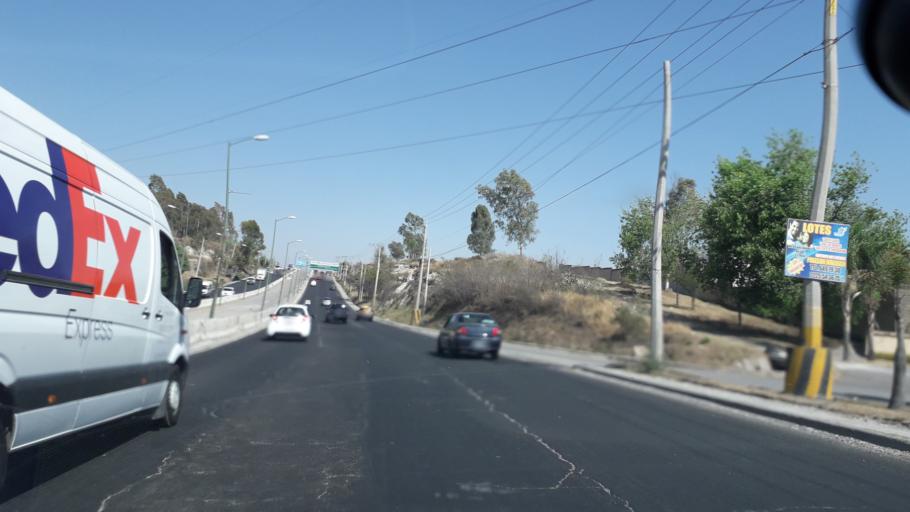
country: MX
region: Puebla
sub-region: Puebla
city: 18 de Marzo
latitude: 18.9728
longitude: -98.2083
